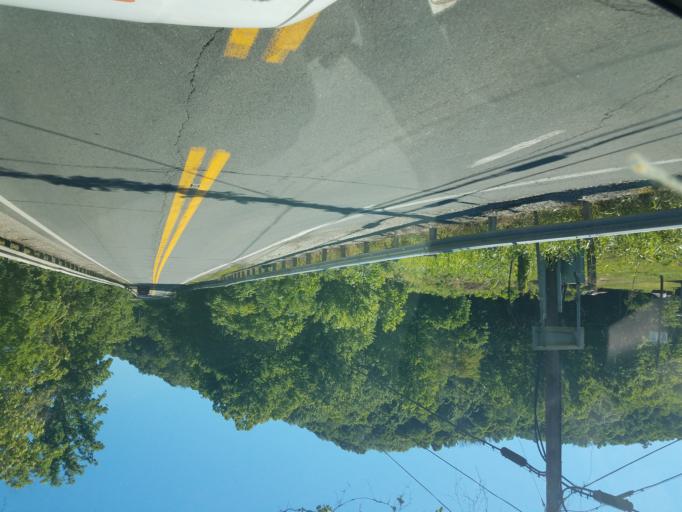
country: US
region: West Virginia
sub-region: Cabell County
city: Lesage
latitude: 38.4685
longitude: -82.3009
